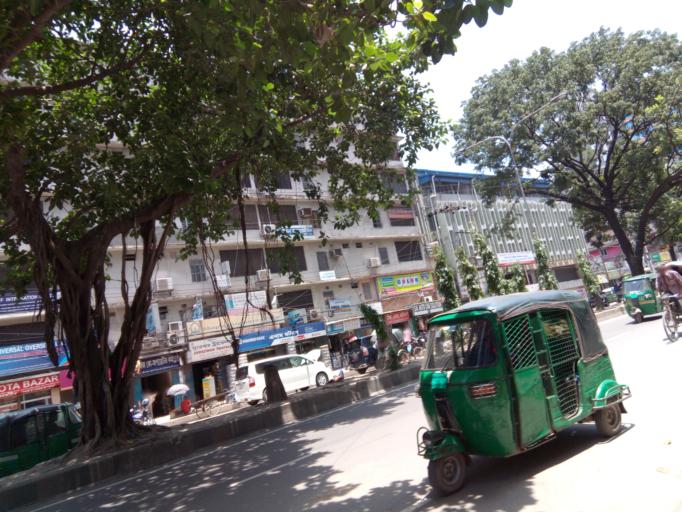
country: BD
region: Dhaka
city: Paltan
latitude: 23.7327
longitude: 90.4103
